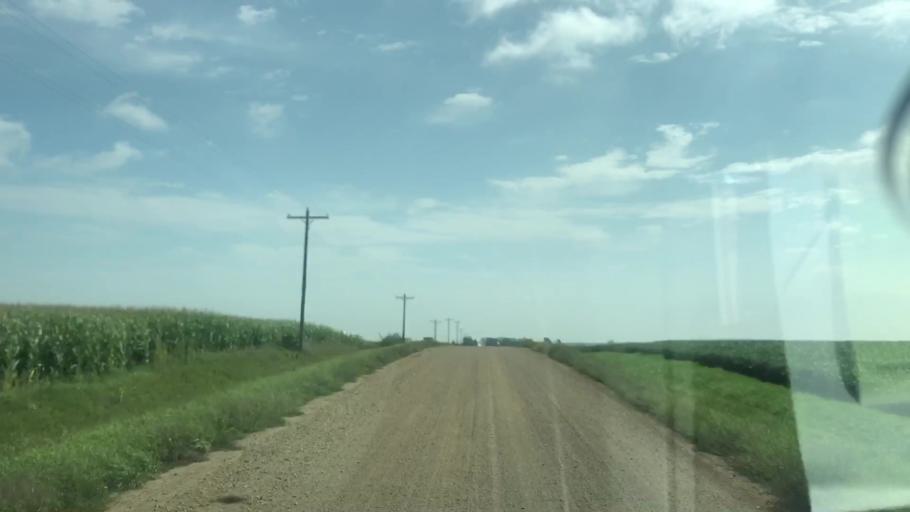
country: US
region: Iowa
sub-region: O'Brien County
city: Sheldon
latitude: 43.2153
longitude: -95.9766
